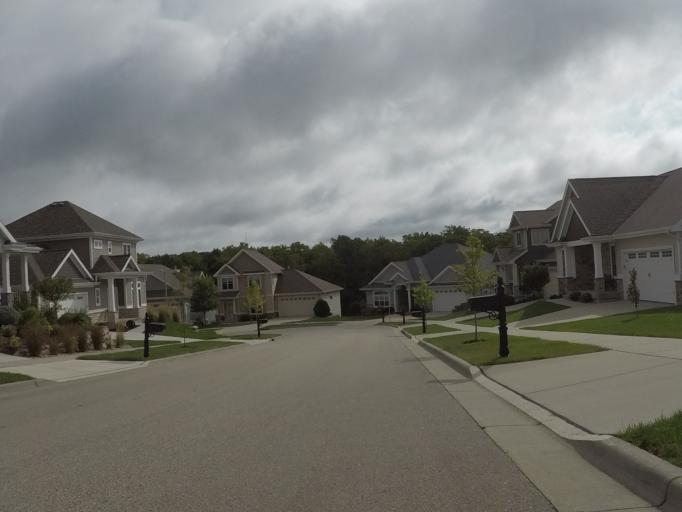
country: US
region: Wisconsin
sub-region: Dane County
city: Verona
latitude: 43.0425
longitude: -89.5392
